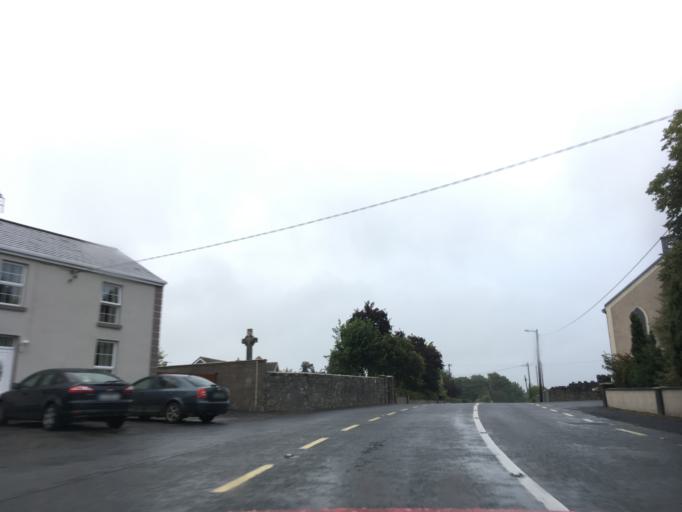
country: IE
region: Munster
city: Tipperary
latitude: 52.4876
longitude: -8.0627
